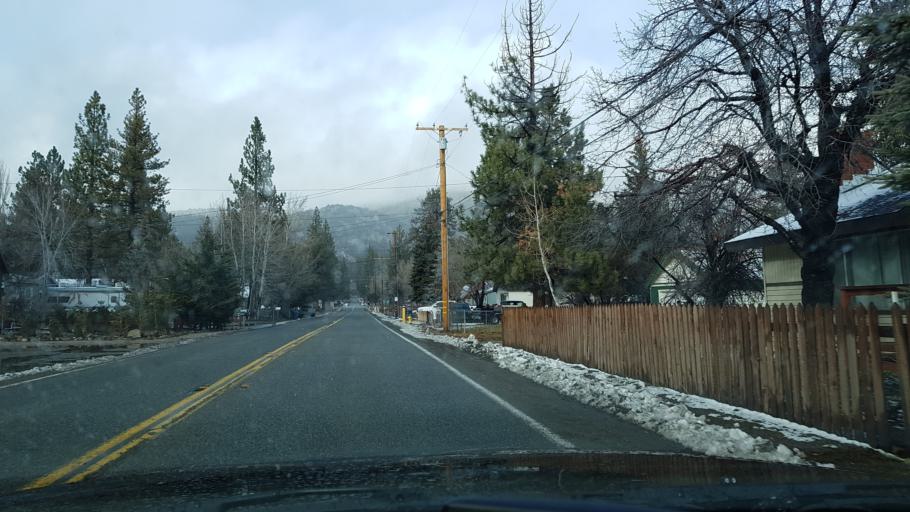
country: US
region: California
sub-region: San Bernardino County
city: Big Bear City
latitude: 34.2677
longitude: -116.8468
